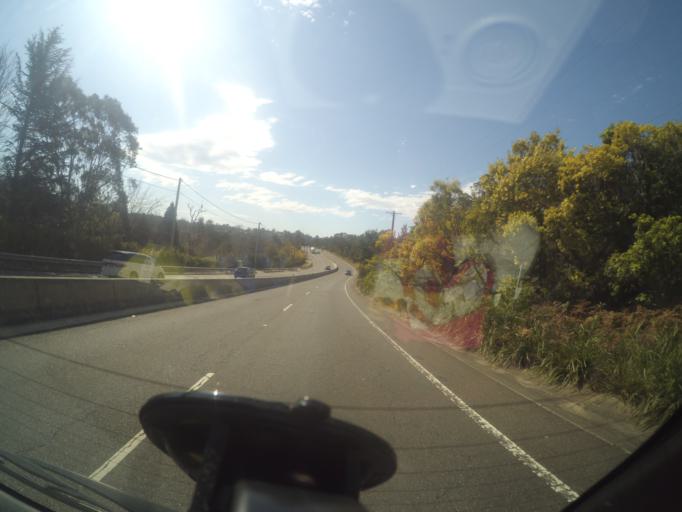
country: AU
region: New South Wales
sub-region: Blue Mountains Municipality
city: Hazelbrook
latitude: -33.7050
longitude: 150.5297
